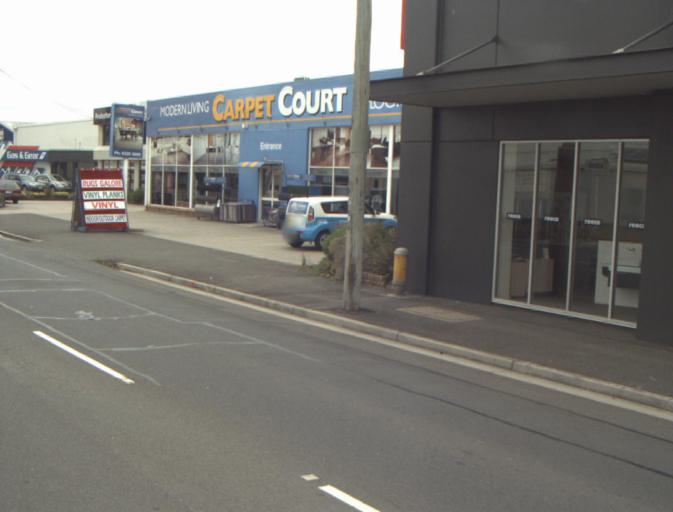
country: AU
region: Tasmania
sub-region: Launceston
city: Newnham
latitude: -41.4130
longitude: 147.1330
